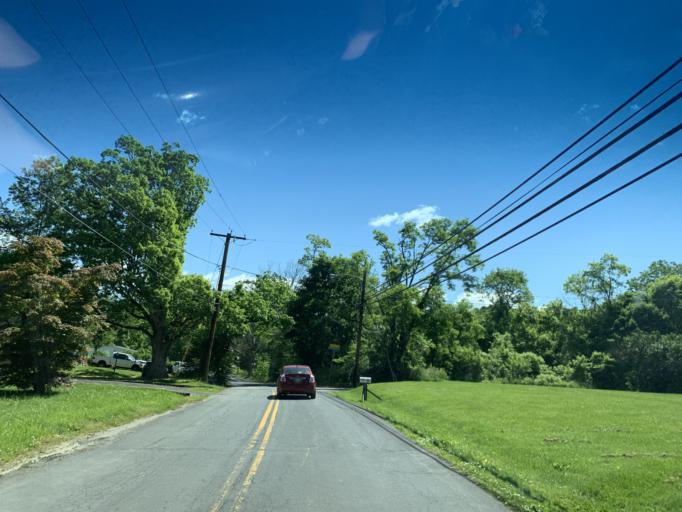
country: US
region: Maryland
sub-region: Harford County
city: South Bel Air
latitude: 39.6389
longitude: -76.2604
